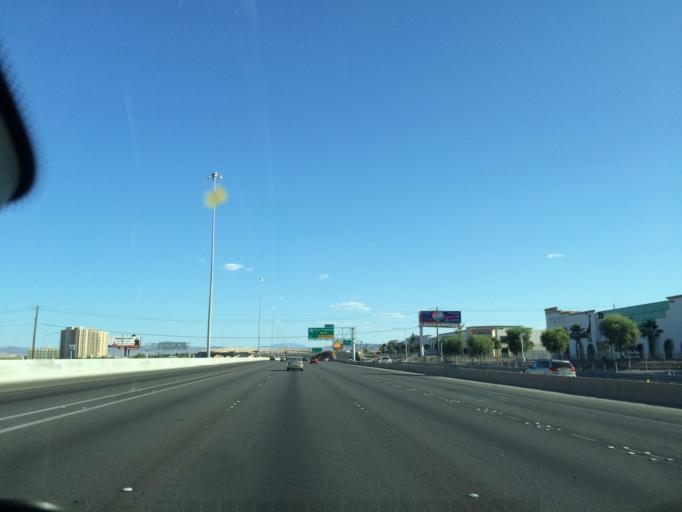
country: US
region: Nevada
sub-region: Clark County
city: Paradise
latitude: 36.0518
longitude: -115.1811
